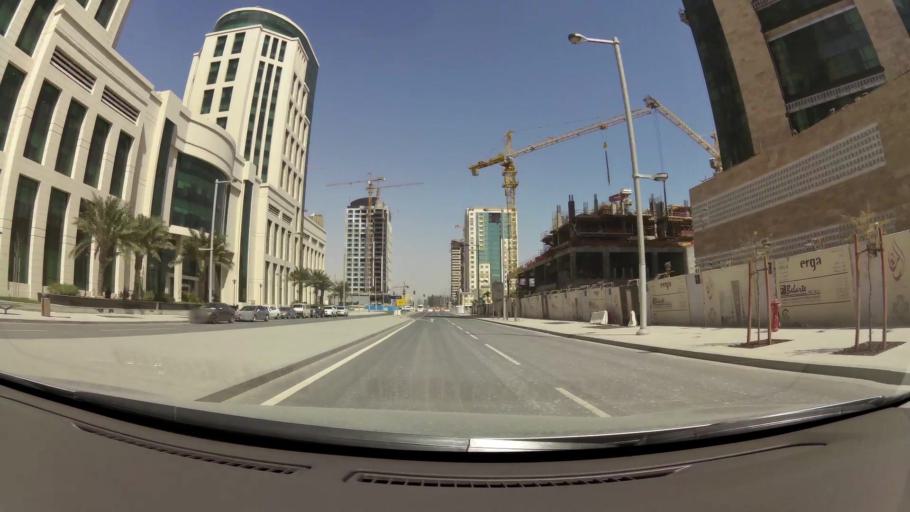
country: QA
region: Baladiyat ad Dawhah
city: Doha
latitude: 25.3931
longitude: 51.5223
